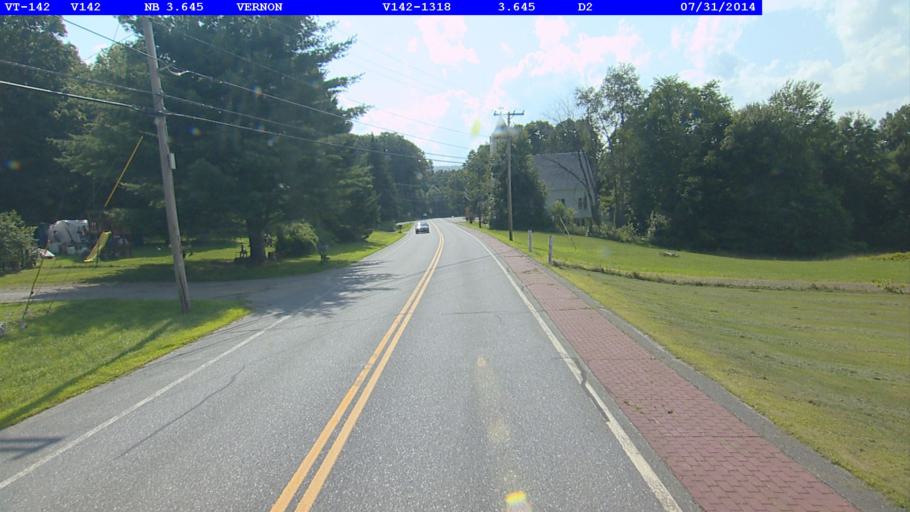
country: US
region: New Hampshire
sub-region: Cheshire County
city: Hinsdale
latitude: 42.7619
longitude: -72.5093
